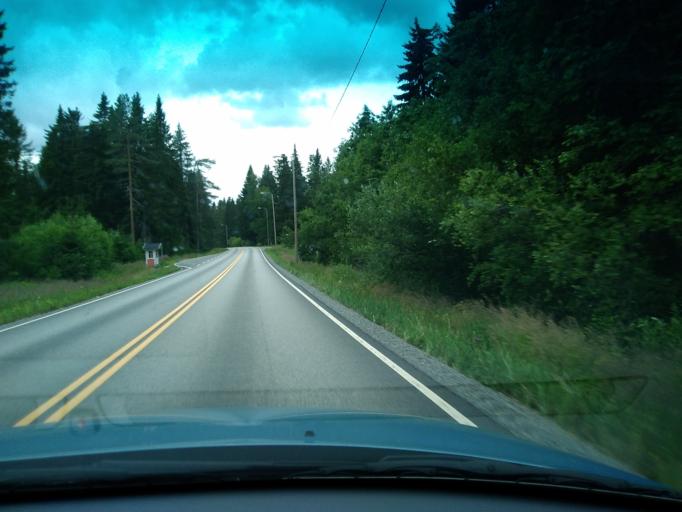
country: FI
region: Central Finland
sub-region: Saarijaervi-Viitasaari
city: Pylkoenmaeki
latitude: 62.6472
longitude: 24.9399
